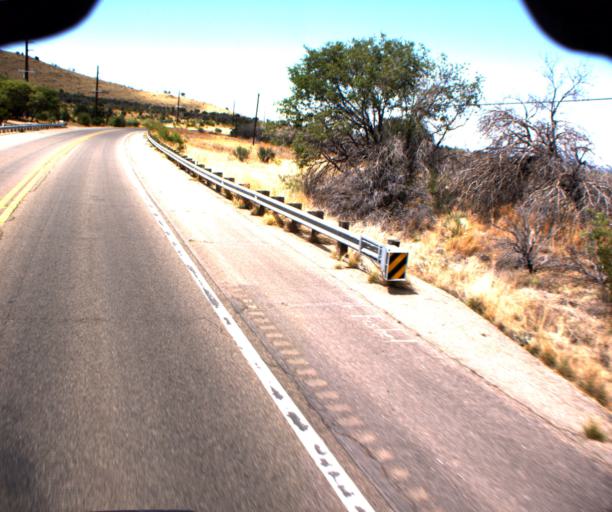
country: US
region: Arizona
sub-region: Cochise County
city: Sierra Vista Southeast
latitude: 31.3986
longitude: -110.2395
